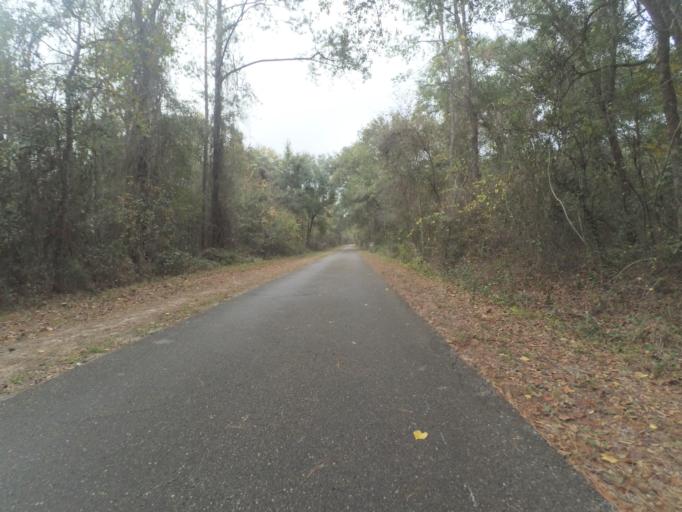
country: US
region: Florida
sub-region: Alachua County
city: Gainesville
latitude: 29.6126
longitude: -82.2558
